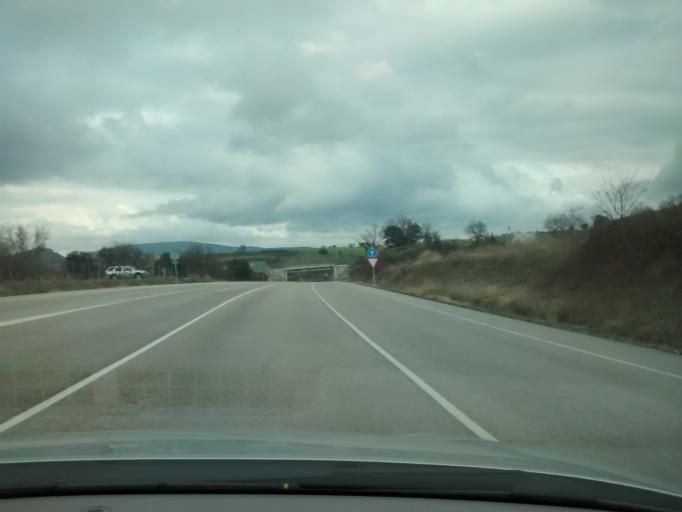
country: ES
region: Castille and Leon
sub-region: Provincia de Burgos
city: Villasana de Mena
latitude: 43.1039
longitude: -3.2695
